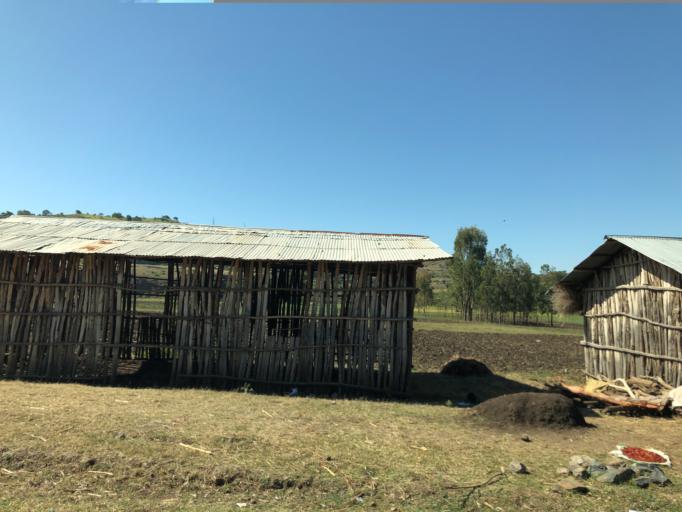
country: ET
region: Amhara
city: Adis Zemen
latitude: 12.1797
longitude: 37.6847
